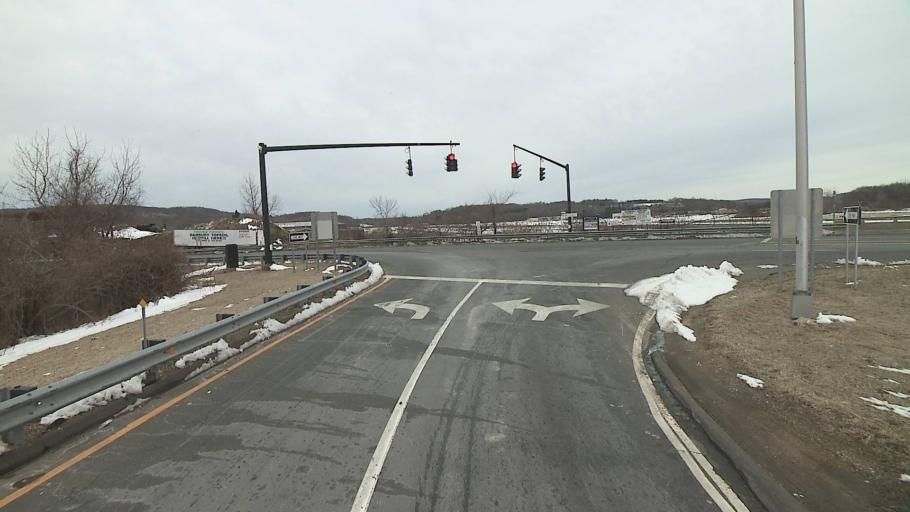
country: US
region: Connecticut
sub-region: Fairfield County
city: Danbury
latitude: 41.3719
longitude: -73.4751
